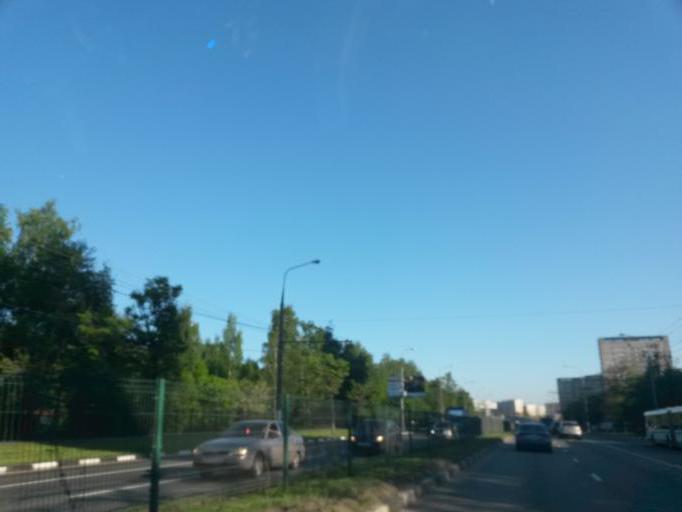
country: RU
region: Moscow
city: Biryulevo
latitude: 55.5959
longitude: 37.6721
